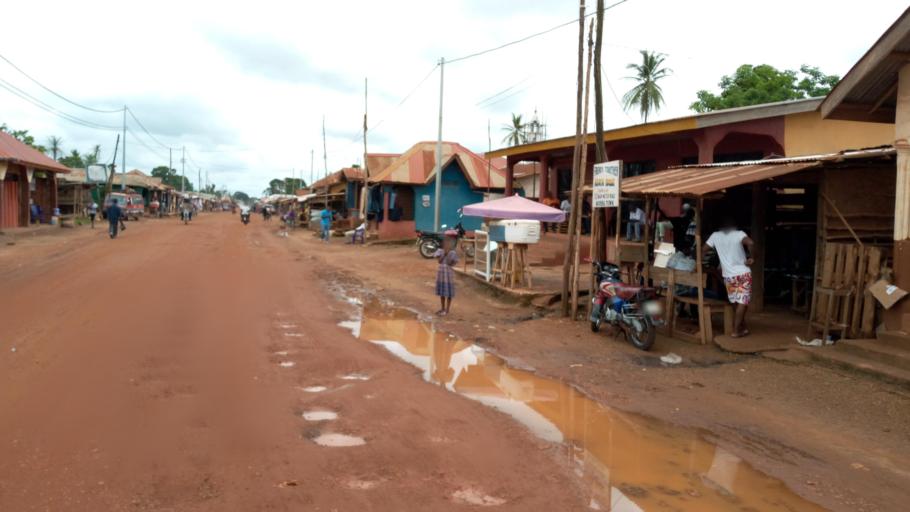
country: SL
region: Southern Province
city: Mogbwemo
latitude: 7.7856
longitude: -12.2972
